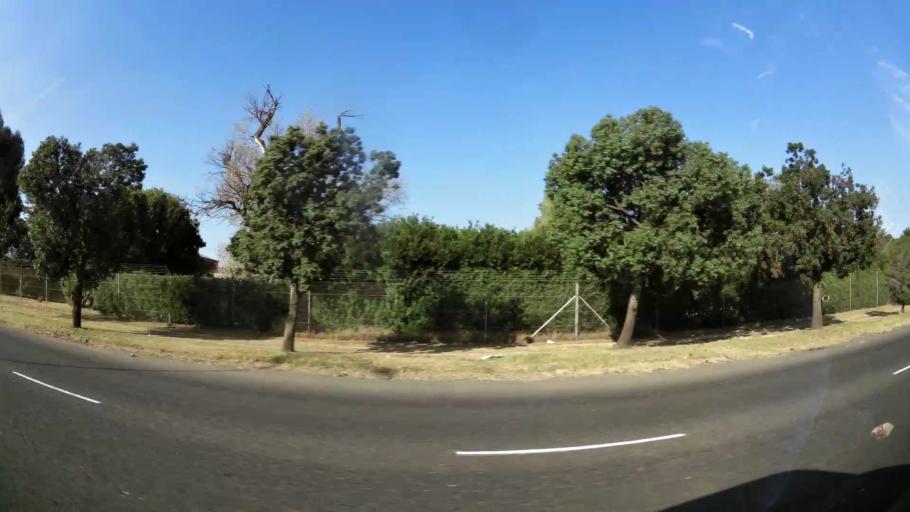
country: ZA
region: Gauteng
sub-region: West Rand District Municipality
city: Randfontein
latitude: -26.1711
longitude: 27.7115
